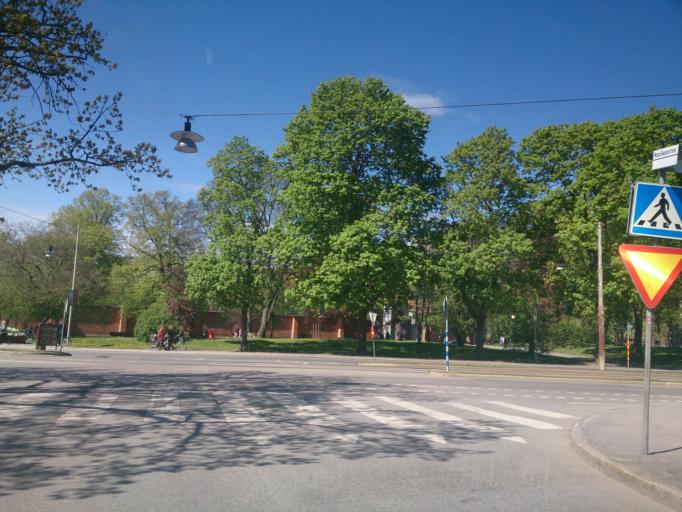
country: SE
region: Stockholm
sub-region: Stockholms Kommun
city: OEstermalm
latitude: 59.3274
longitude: 18.0971
